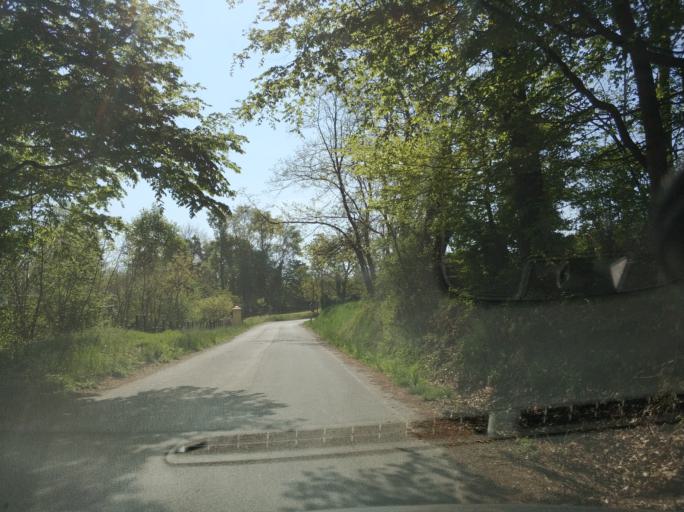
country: IT
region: Piedmont
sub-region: Provincia di Torino
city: Vauda Canavese Superiore
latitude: 45.2746
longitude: 7.6342
